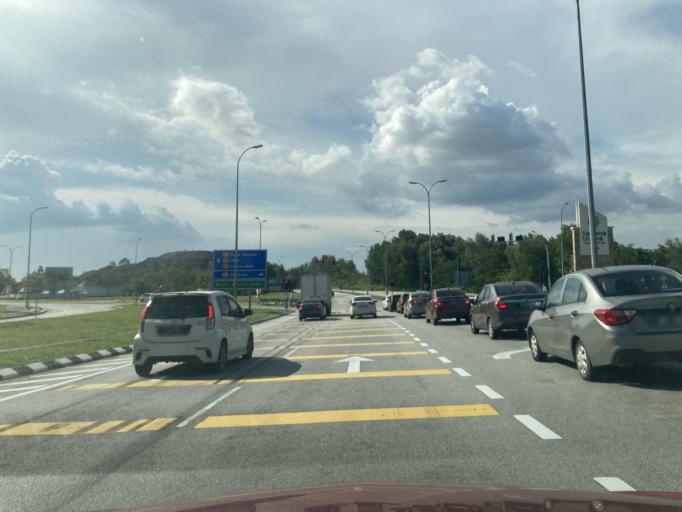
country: MY
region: Selangor
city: Kampung Baru Subang
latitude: 3.2011
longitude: 101.4642
